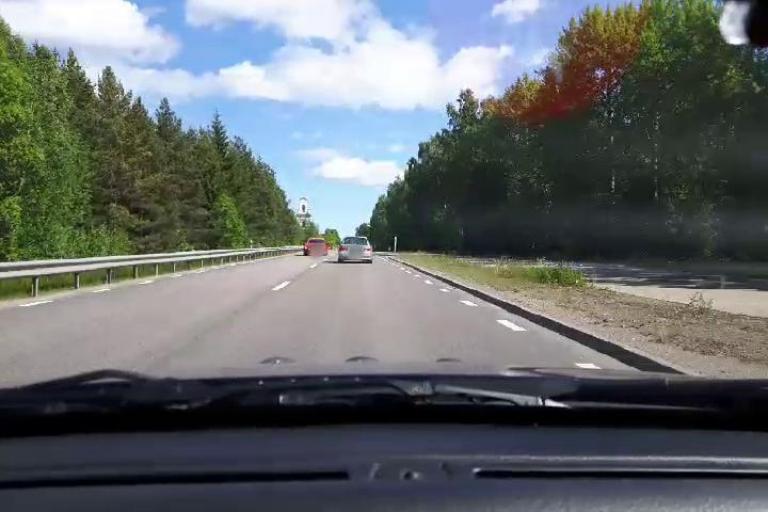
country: SE
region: Gaevleborg
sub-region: Hudiksvalls Kommun
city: Sorforsa
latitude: 61.7352
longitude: 16.9314
